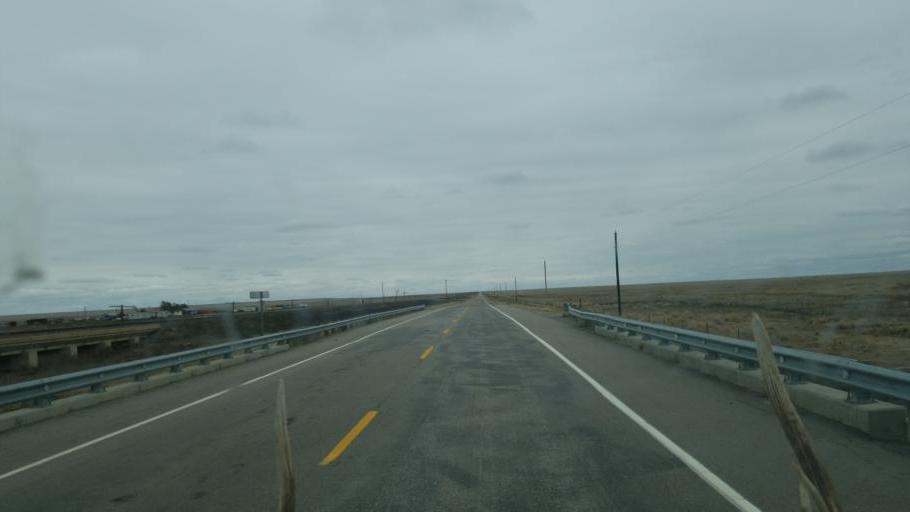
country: US
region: Colorado
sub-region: Crowley County
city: Ordway
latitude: 38.2469
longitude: -103.5975
